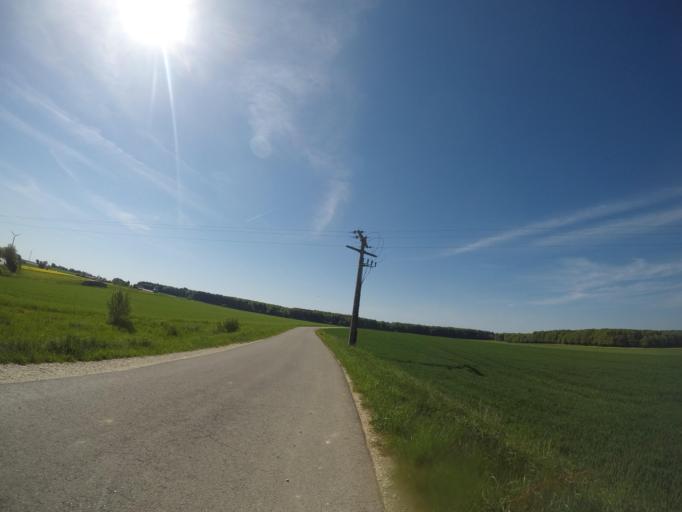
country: DE
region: Baden-Wuerttemberg
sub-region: Tuebingen Region
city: Laichingen
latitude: 48.4550
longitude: 9.7071
